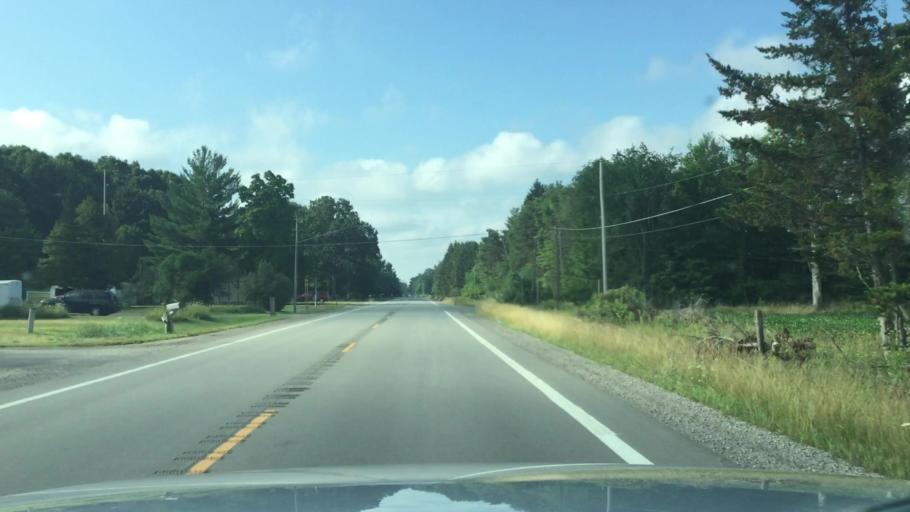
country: US
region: Michigan
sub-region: Genesee County
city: Clio
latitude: 43.2292
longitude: -83.7352
